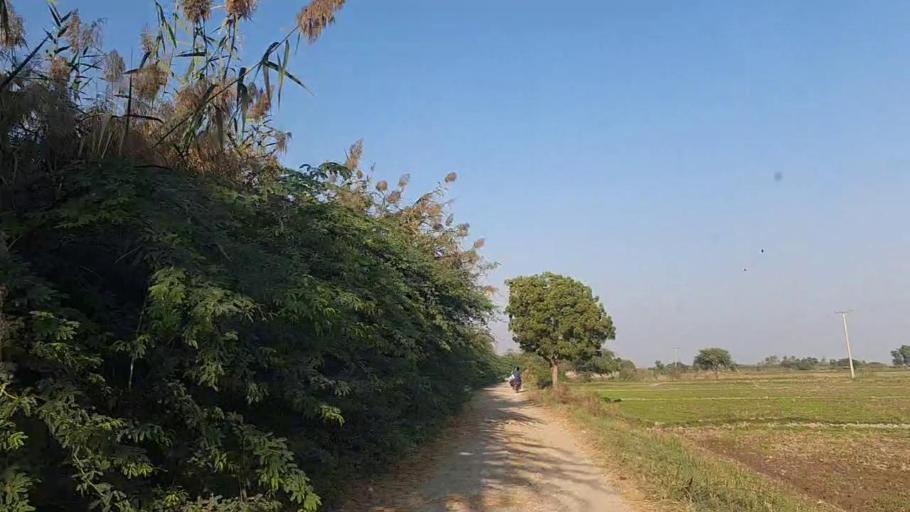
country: PK
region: Sindh
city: Thatta
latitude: 24.7205
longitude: 67.9447
